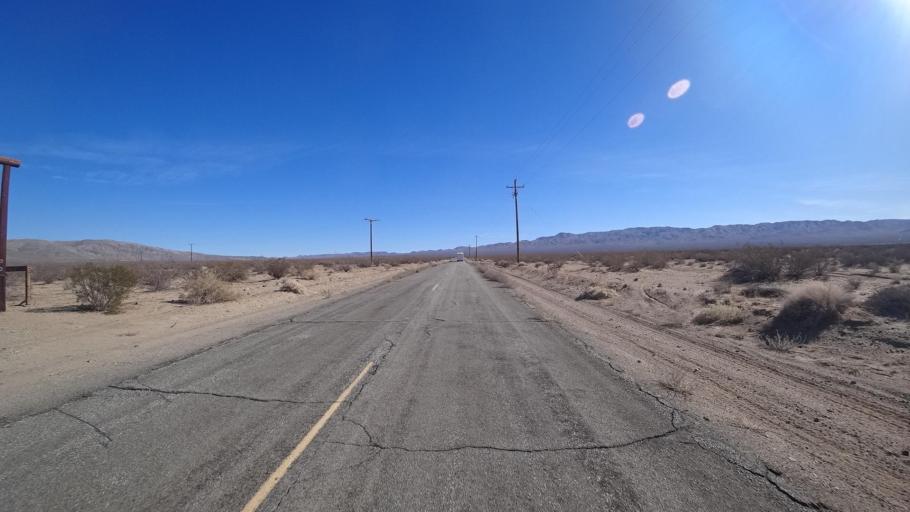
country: US
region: California
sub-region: Kern County
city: China Lake Acres
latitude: 35.3915
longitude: -117.7897
